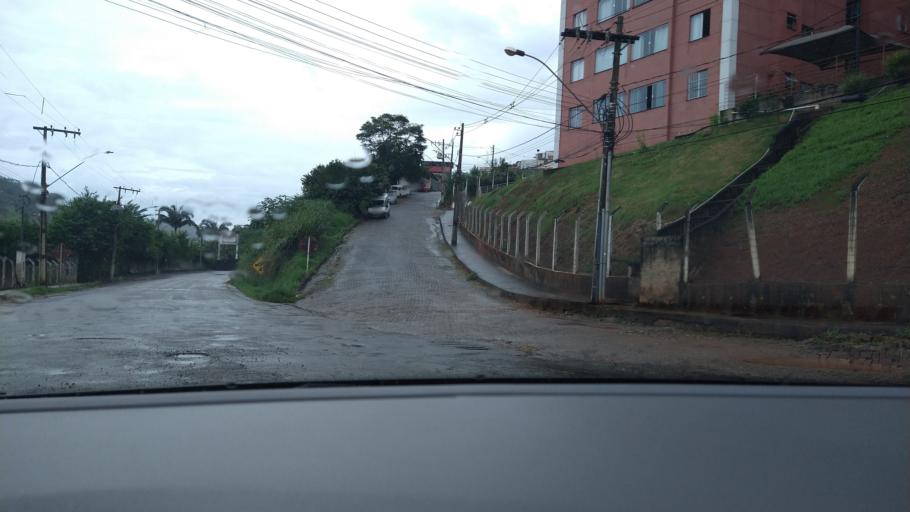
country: BR
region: Minas Gerais
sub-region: Ponte Nova
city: Ponte Nova
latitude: -20.3986
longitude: -42.9005
